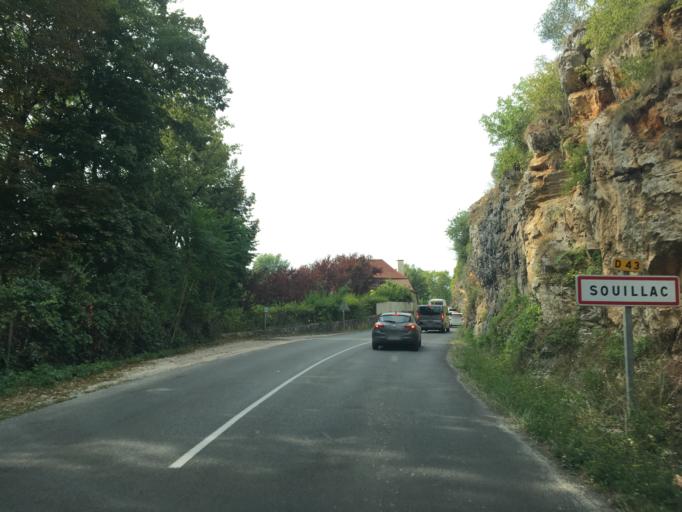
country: FR
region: Midi-Pyrenees
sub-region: Departement du Lot
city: Souillac
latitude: 44.8827
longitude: 1.4872
